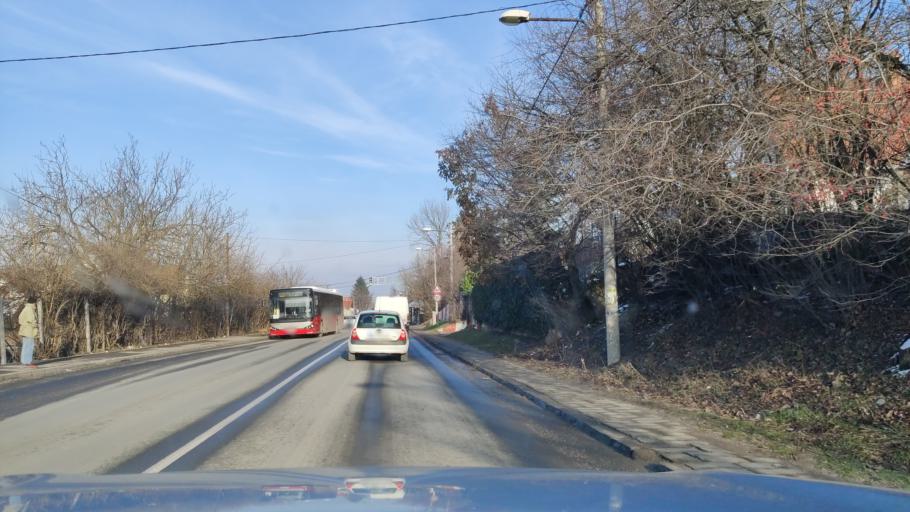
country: RS
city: Rusanj
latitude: 44.7010
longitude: 20.5042
